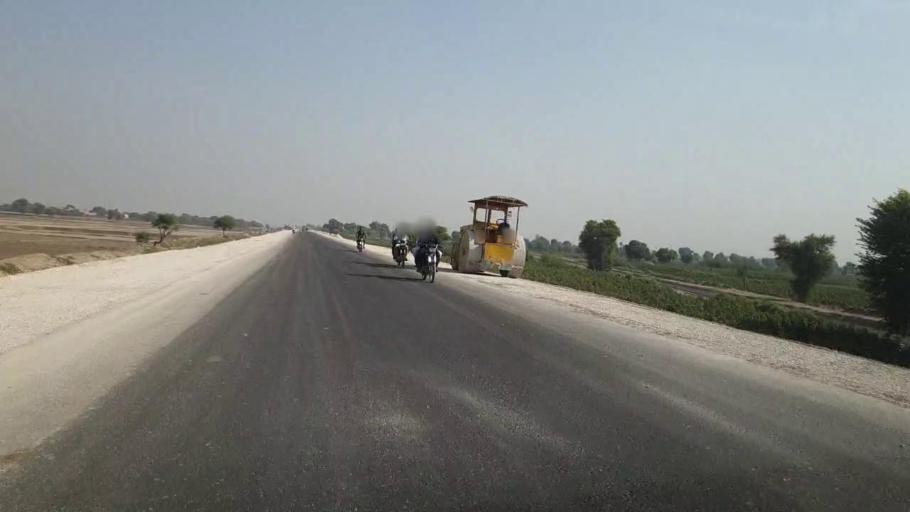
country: PK
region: Sindh
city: Bhan
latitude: 26.5521
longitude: 67.7798
